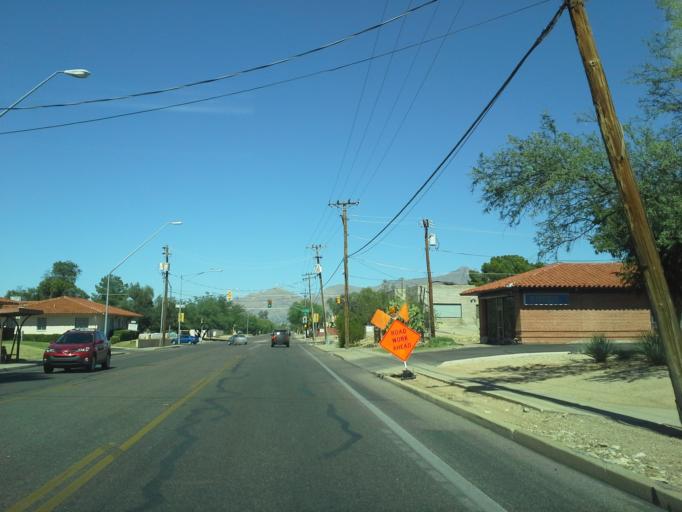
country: US
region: Arizona
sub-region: Pima County
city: Tucson
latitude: 32.2418
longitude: -110.9353
